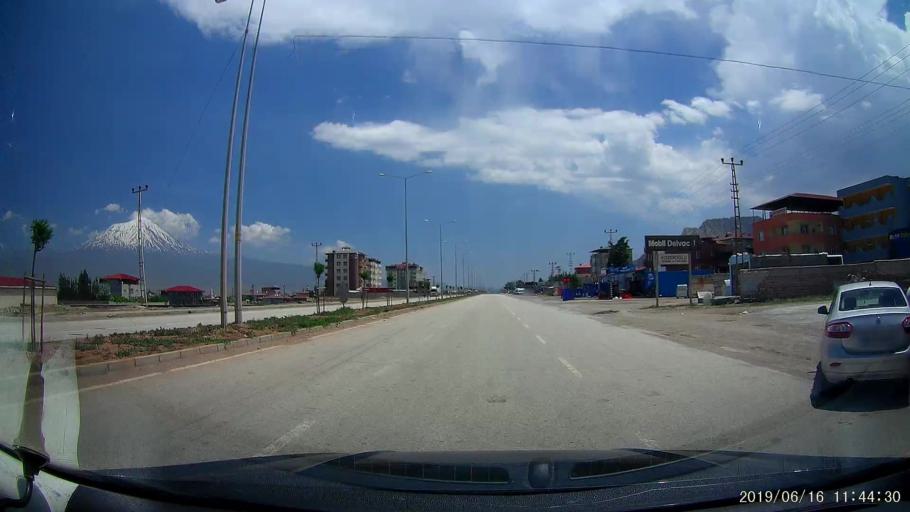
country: TR
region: Agri
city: Dogubayazit
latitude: 39.5573
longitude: 44.0897
